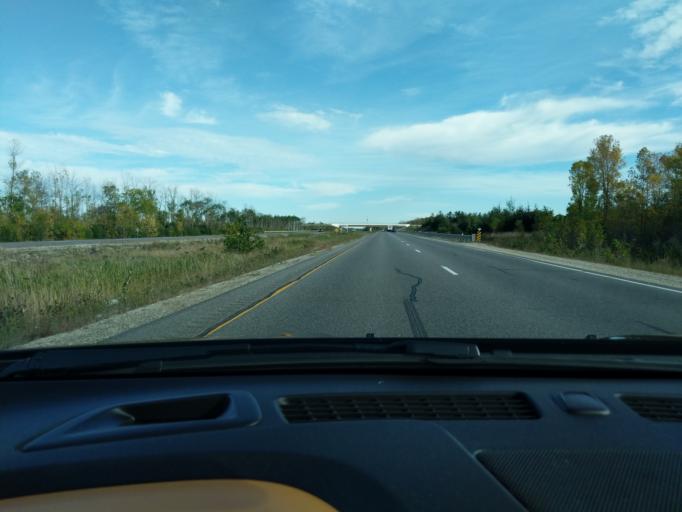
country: CA
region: Ontario
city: Collingwood
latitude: 44.4726
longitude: -80.1466
